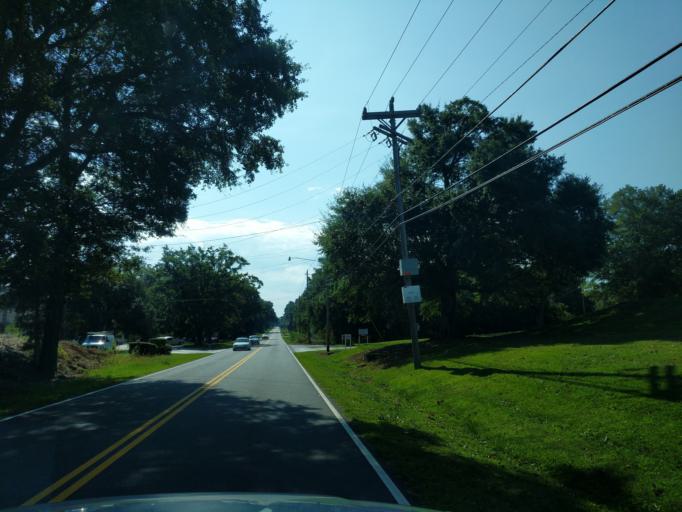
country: US
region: South Carolina
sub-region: Spartanburg County
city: Wellford
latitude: 34.9522
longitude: -82.1117
